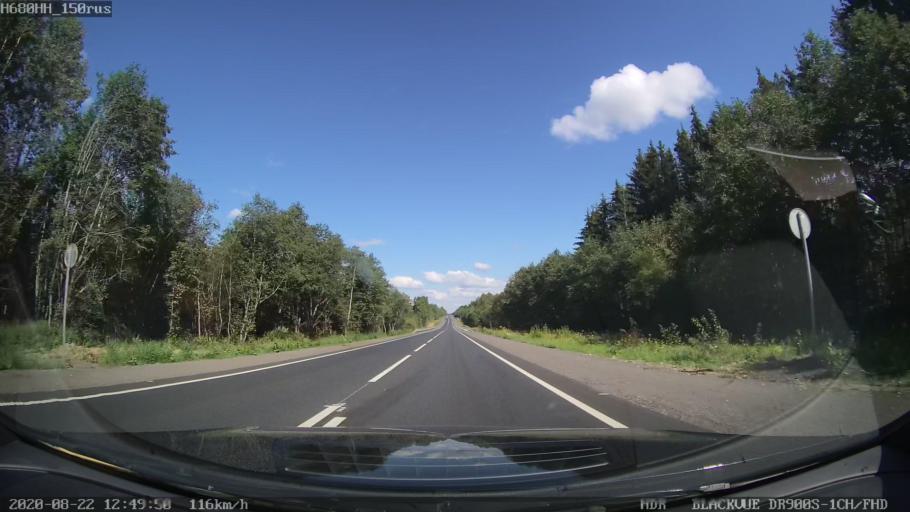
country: RU
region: Tverskaya
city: Rameshki
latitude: 57.4572
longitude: 36.2121
